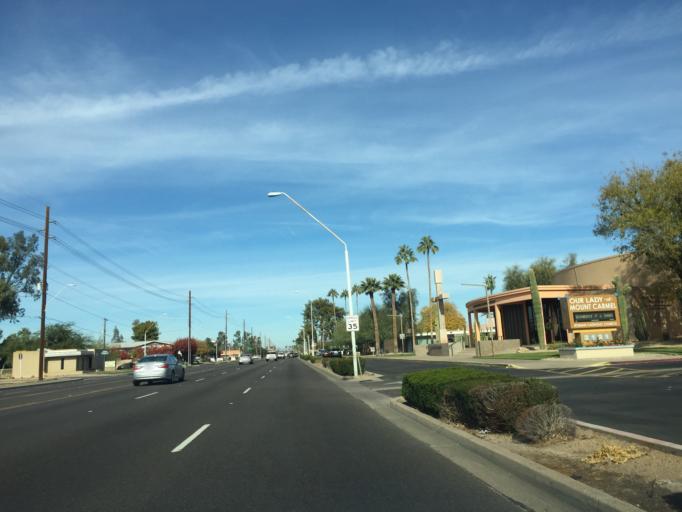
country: US
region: Arizona
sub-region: Maricopa County
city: Tempe
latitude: 33.4041
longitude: -111.9262
